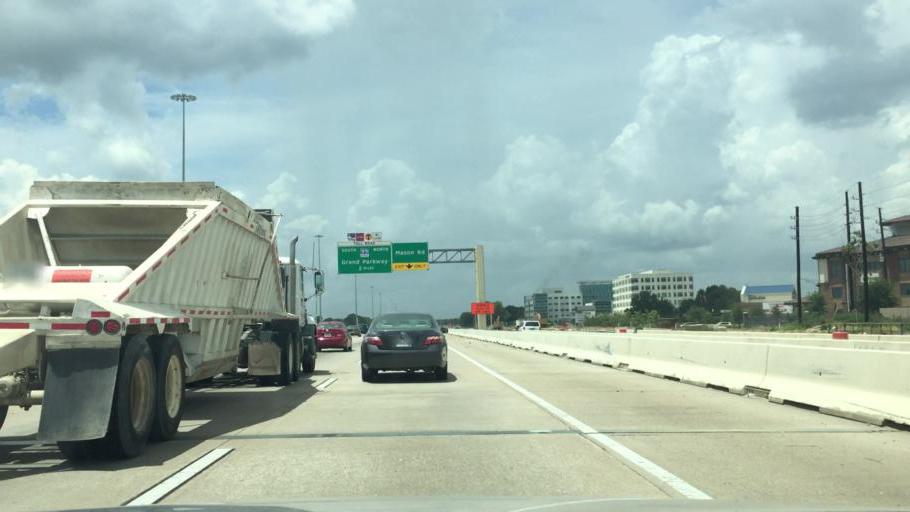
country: US
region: Texas
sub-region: Harris County
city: Cypress
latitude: 29.9812
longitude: -95.7270
